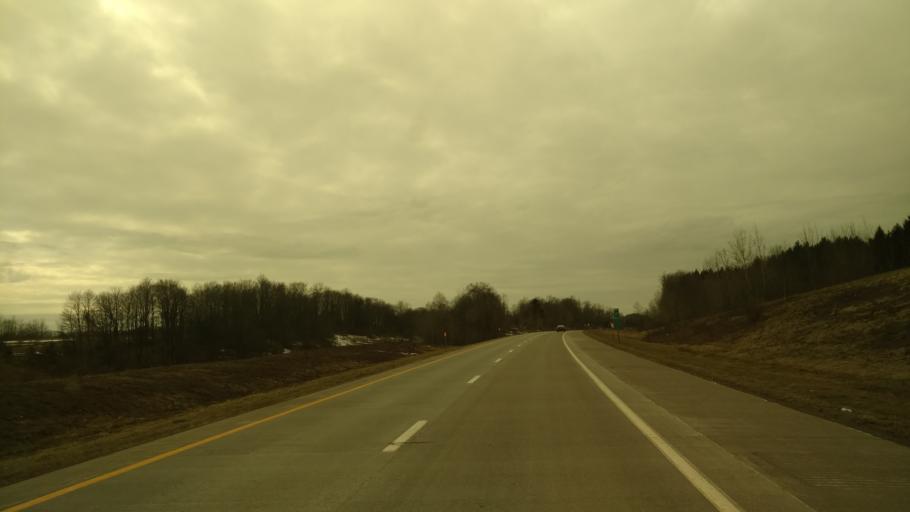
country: US
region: New York
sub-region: Chautauqua County
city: Lakewood
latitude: 42.1532
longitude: -79.4382
